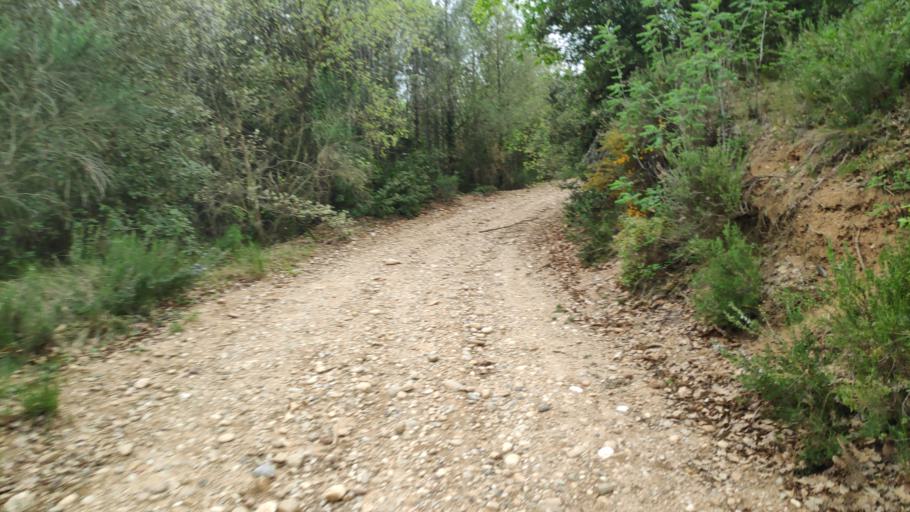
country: ES
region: Catalonia
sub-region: Provincia de Barcelona
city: Sant Quirze del Valles
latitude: 41.5305
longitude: 2.0636
